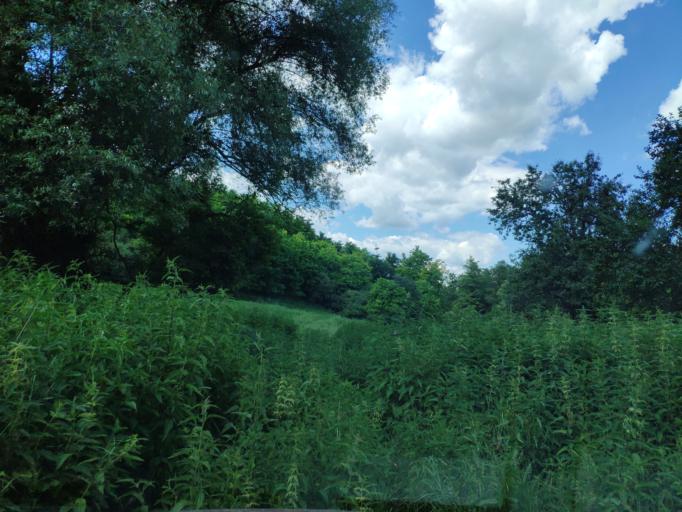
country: HU
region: Borsod-Abauj-Zemplen
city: Arlo
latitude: 48.2556
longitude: 20.1688
